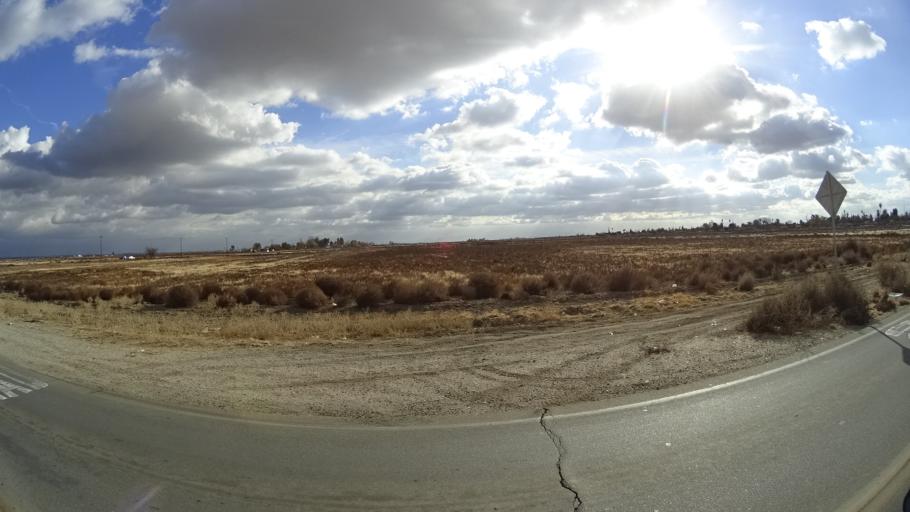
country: US
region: California
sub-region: Kern County
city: Greenfield
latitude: 35.3104
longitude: -118.9870
